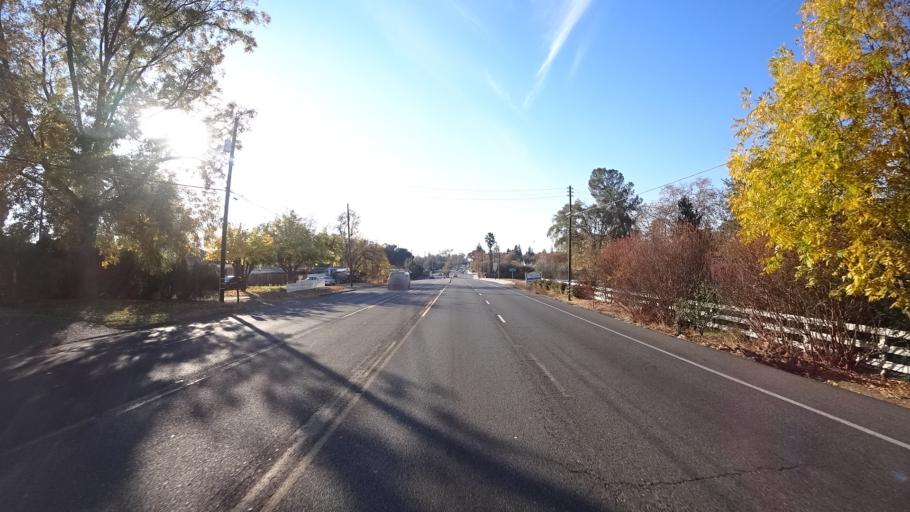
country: US
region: California
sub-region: Sacramento County
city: Citrus Heights
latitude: 38.7209
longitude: -121.2720
